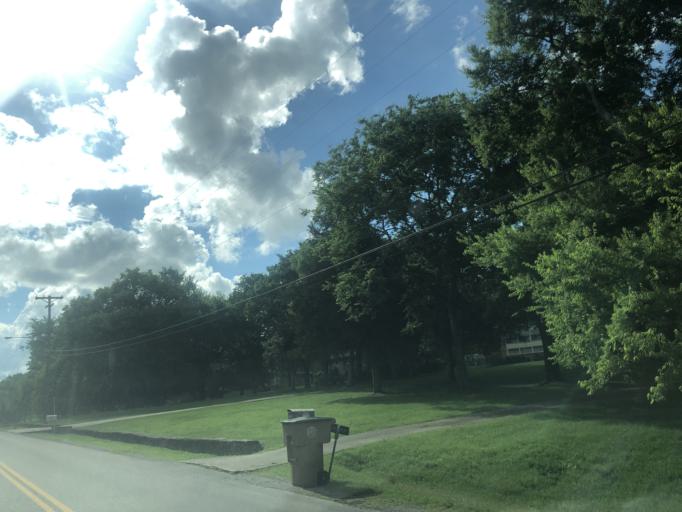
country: US
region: Tennessee
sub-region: Davidson County
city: Nashville
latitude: 36.2127
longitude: -86.8524
